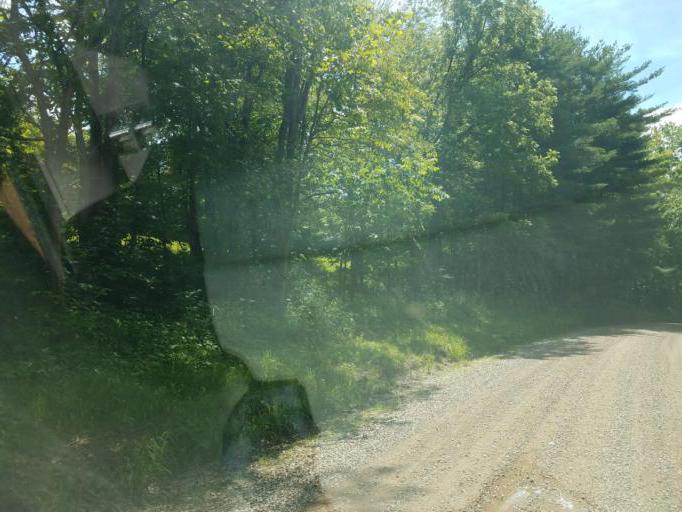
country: US
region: Ohio
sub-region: Knox County
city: Danville
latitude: 40.4284
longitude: -82.2910
